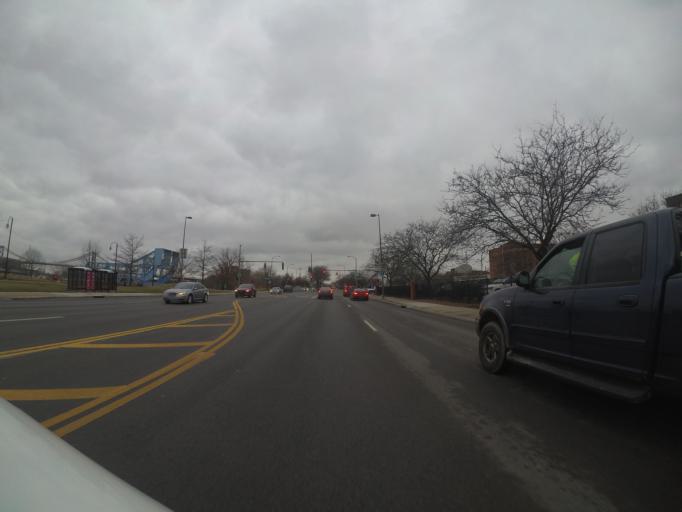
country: US
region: Ohio
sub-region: Lucas County
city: Toledo
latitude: 41.6476
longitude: -83.5367
